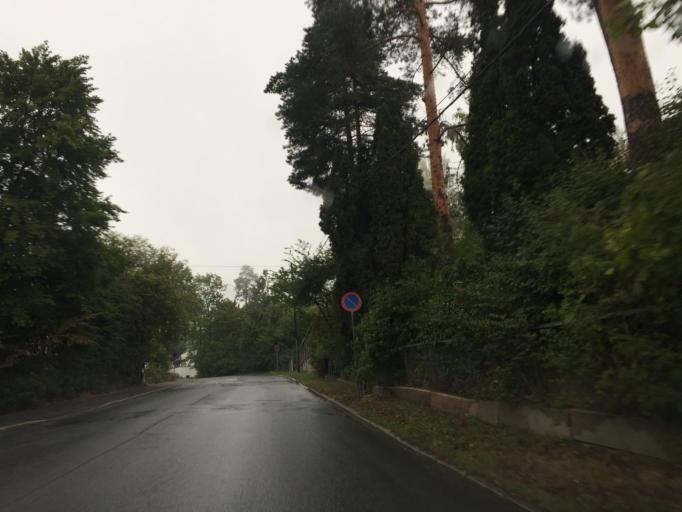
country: NO
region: Oslo
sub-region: Oslo
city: Sjolyststranda
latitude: 59.9545
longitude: 10.6910
